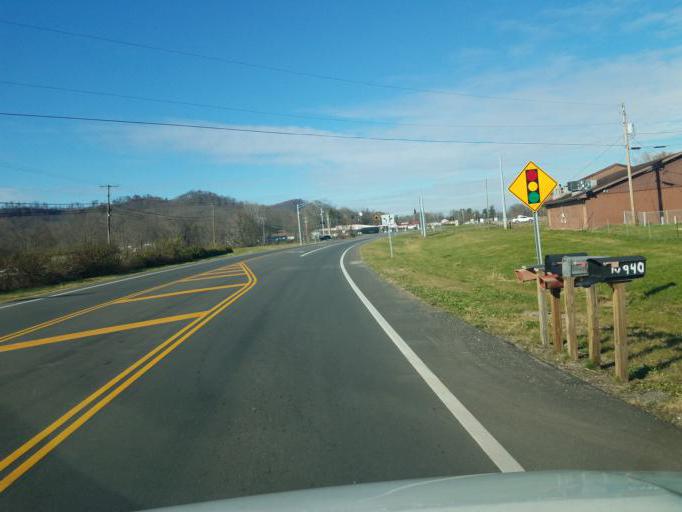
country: US
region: Ohio
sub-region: Scioto County
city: Lucasville
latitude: 38.8798
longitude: -83.0190
